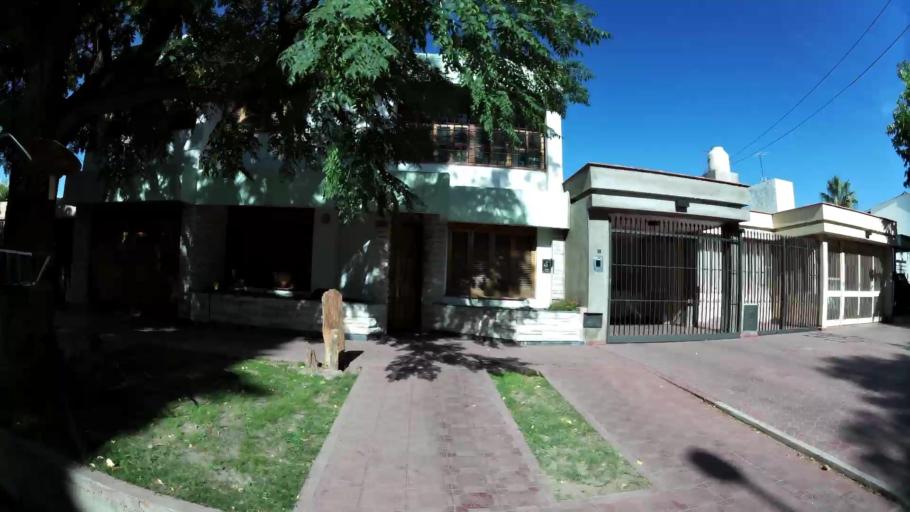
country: AR
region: Mendoza
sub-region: Departamento de Godoy Cruz
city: Godoy Cruz
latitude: -32.9245
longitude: -68.8321
